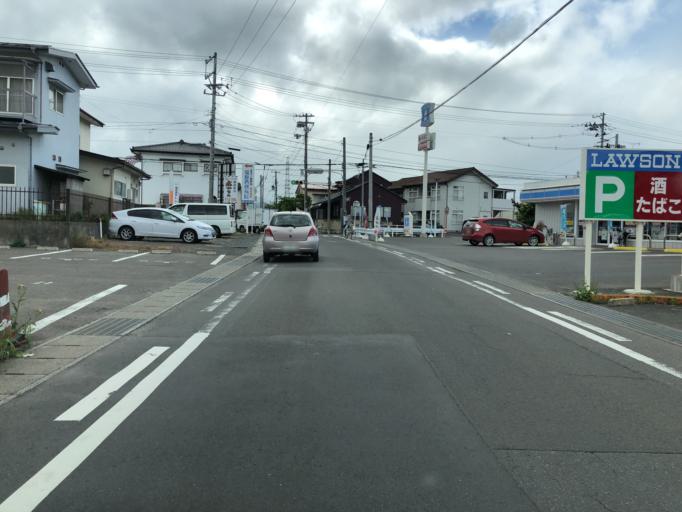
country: JP
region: Fukushima
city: Fukushima-shi
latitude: 37.7678
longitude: 140.4444
